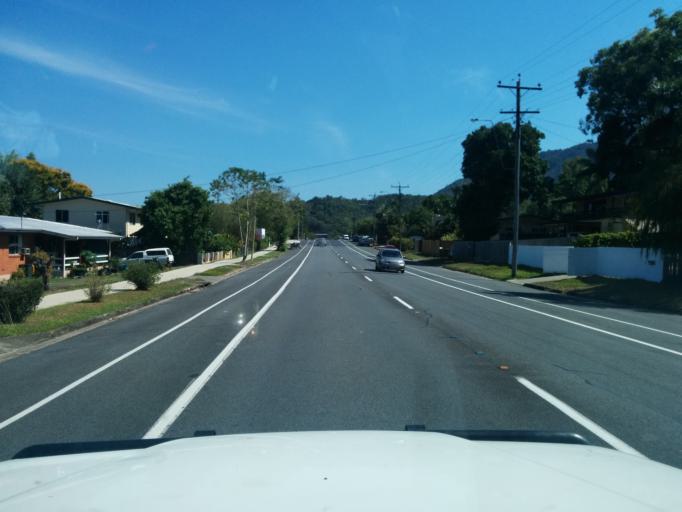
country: AU
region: Queensland
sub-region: Cairns
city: Redlynch
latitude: -16.9062
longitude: 145.7286
